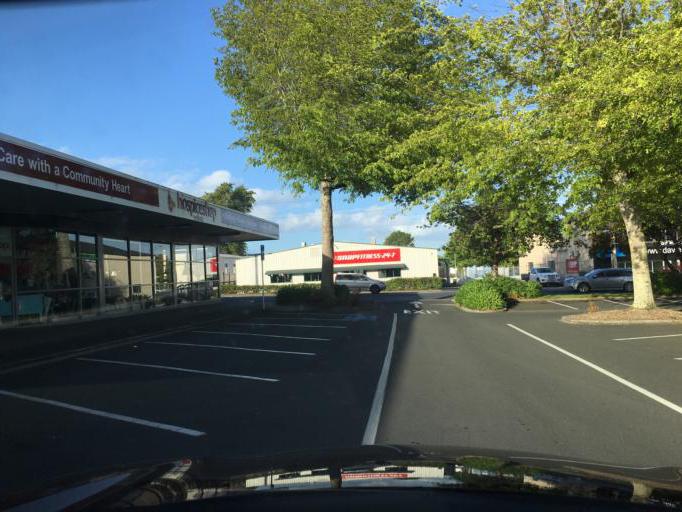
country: NZ
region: Waikato
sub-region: Waipa District
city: Cambridge
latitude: -38.0106
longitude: 175.3276
